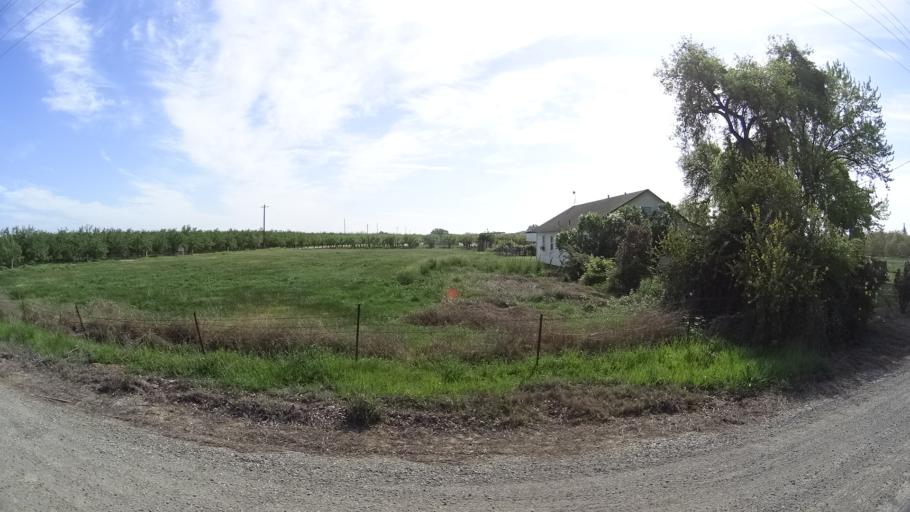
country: US
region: California
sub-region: Glenn County
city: Hamilton City
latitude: 39.6464
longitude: -122.0076
